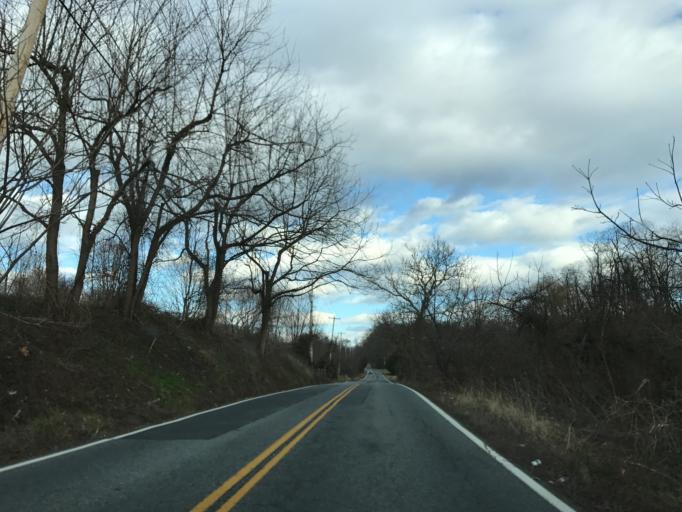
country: US
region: Maryland
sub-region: Cecil County
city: Rising Sun
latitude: 39.6342
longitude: -76.0360
